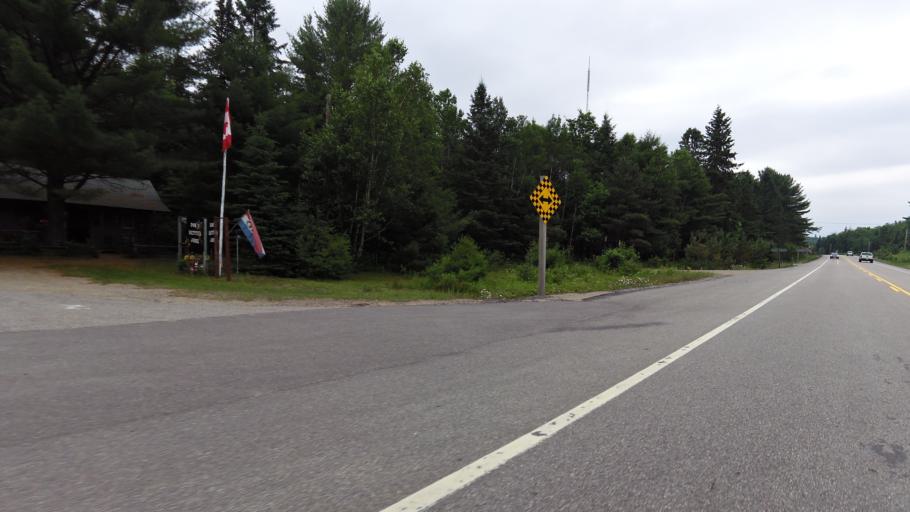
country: CA
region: Ontario
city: Huntsville
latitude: 45.3248
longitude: -78.9719
